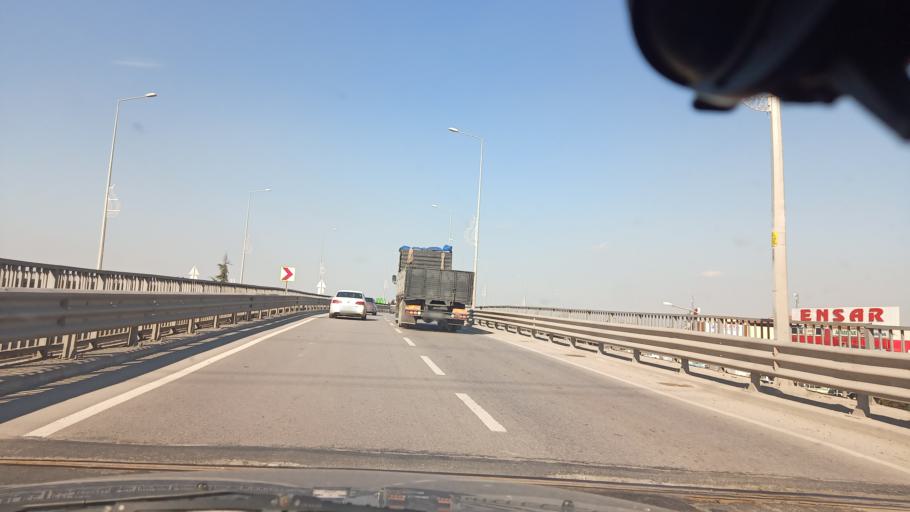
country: TR
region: Sakarya
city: Adapazari
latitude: 40.7483
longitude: 30.4150
